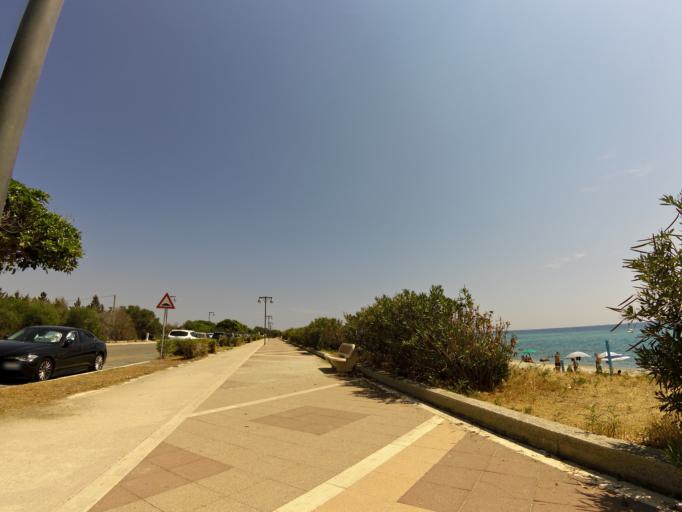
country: IT
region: Calabria
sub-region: Provincia di Reggio Calabria
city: Roccella Ionica
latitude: 38.3256
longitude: 16.4204
